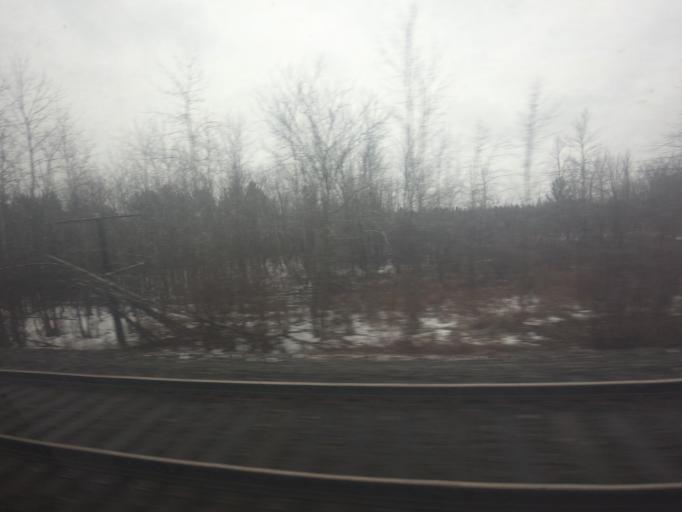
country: CA
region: Ontario
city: Kingston
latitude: 44.2320
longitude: -76.6889
